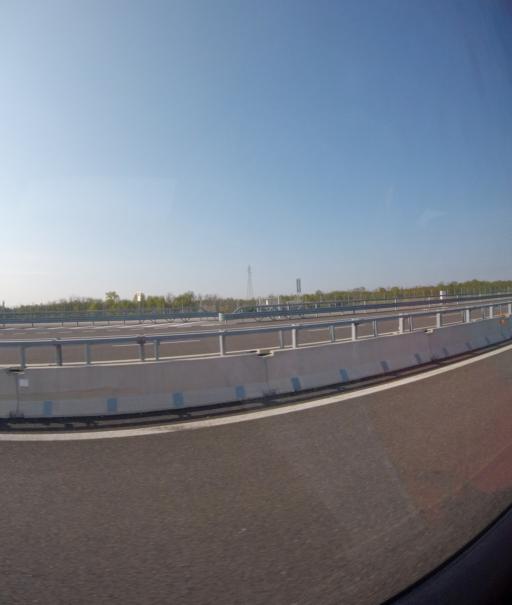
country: IT
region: Lombardy
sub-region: Provincia di Como
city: Mozzate
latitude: 45.6607
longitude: 8.9540
